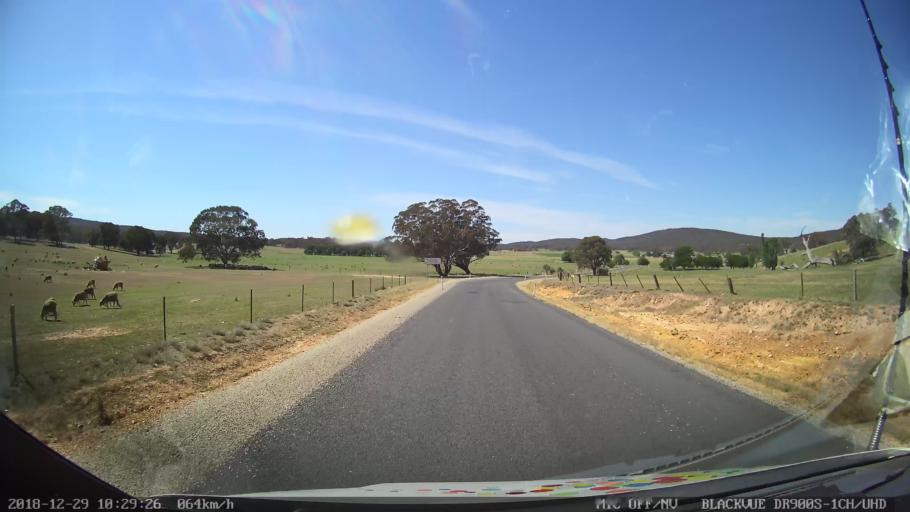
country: AU
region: New South Wales
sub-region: Yass Valley
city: Gundaroo
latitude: -34.9518
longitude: 149.4575
